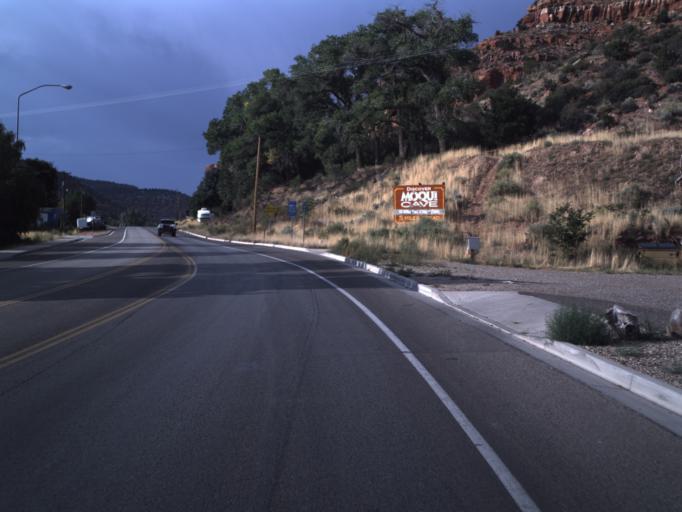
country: US
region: Utah
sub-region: Kane County
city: Kanab
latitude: 37.0540
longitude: -112.5350
